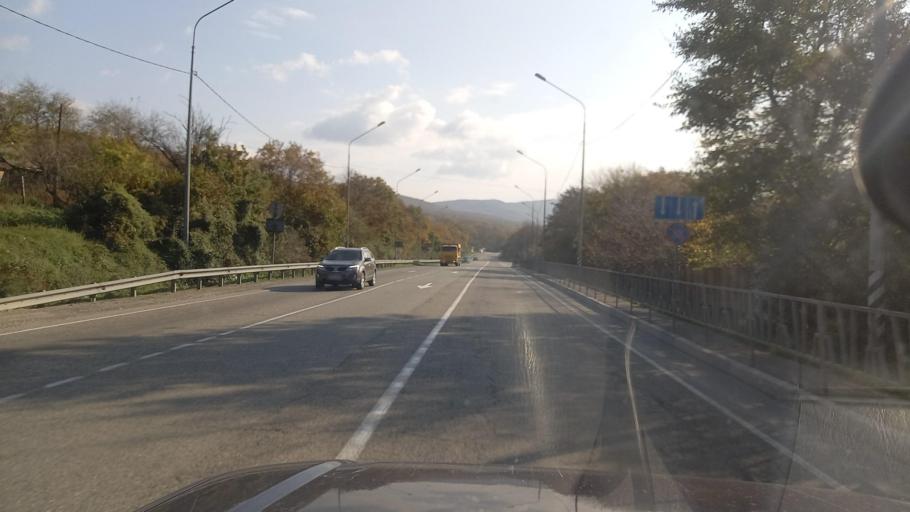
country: RU
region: Krasnodarskiy
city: Verkhnebakanskiy
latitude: 44.8459
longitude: 37.6800
